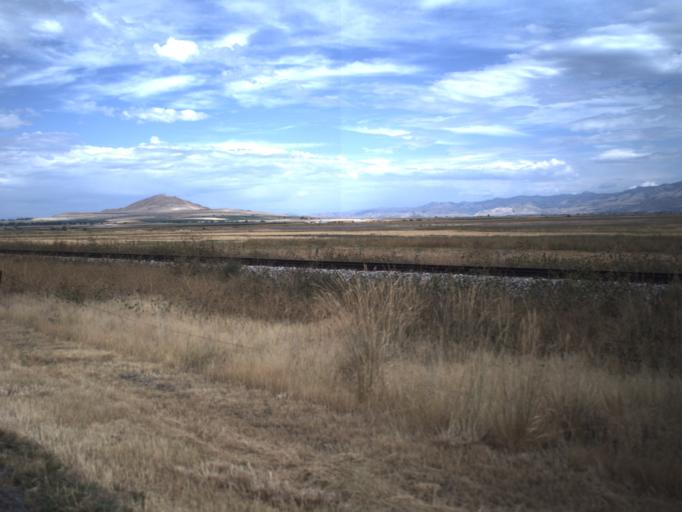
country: US
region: Utah
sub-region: Cache County
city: Benson
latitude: 41.7979
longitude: -111.9910
